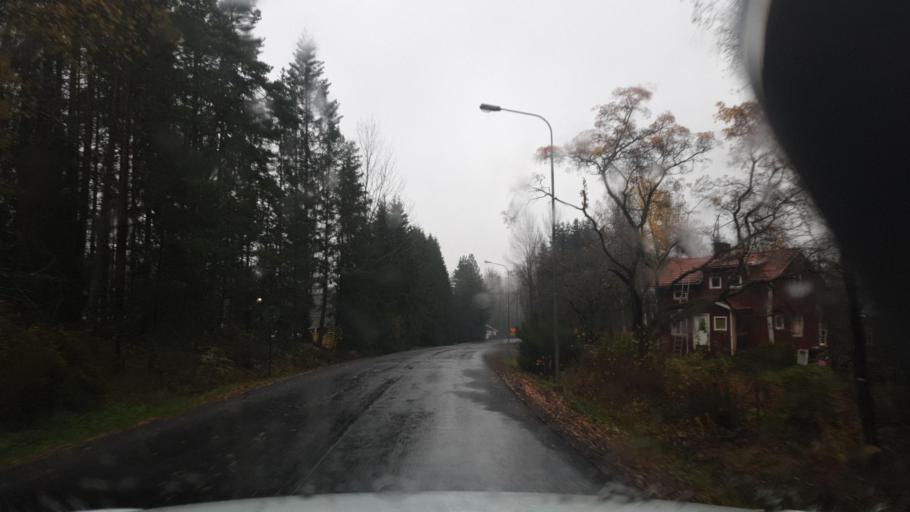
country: SE
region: Vaermland
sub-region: Karlstads Kommun
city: Valberg
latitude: 59.4098
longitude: 13.1795
